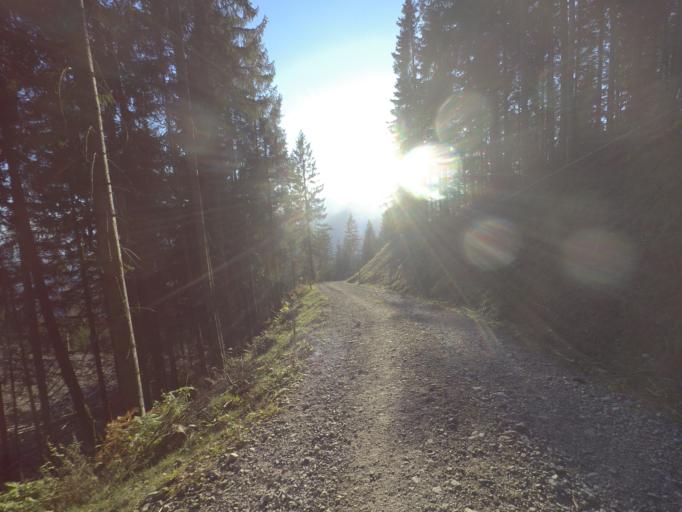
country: AT
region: Salzburg
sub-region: Politischer Bezirk Sankt Johann im Pongau
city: Werfenweng
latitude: 47.4843
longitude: 13.2275
